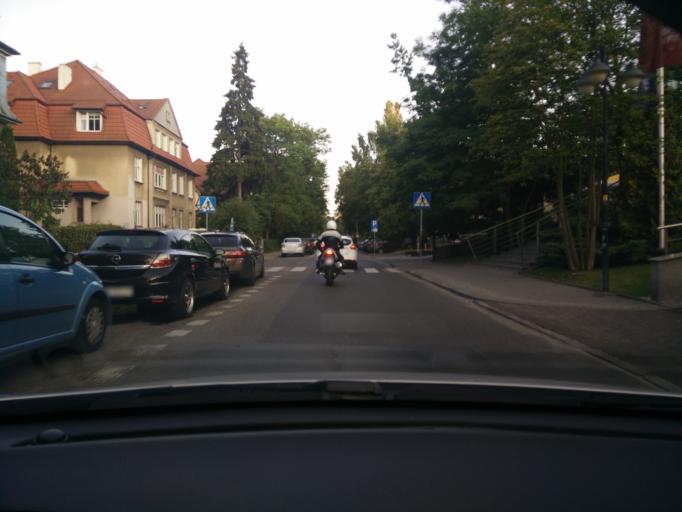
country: PL
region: Pomeranian Voivodeship
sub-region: Sopot
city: Sopot
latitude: 54.4510
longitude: 18.5617
